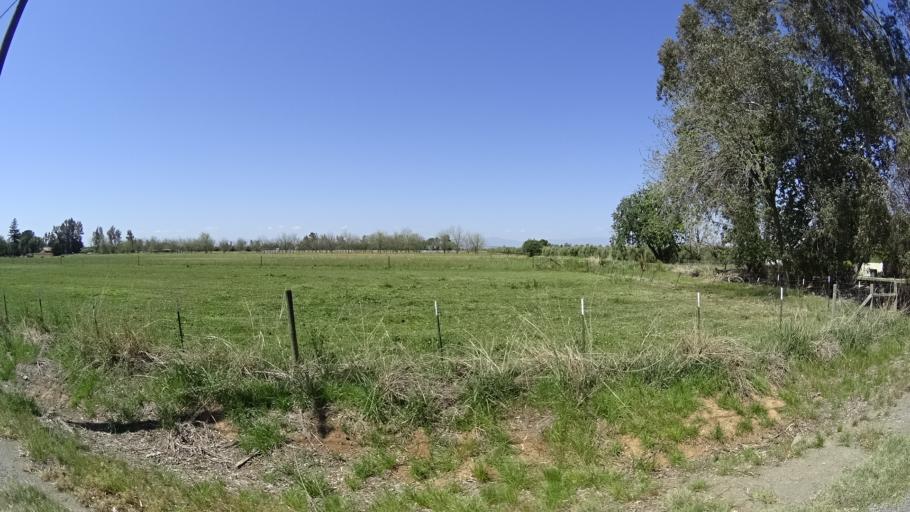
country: US
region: California
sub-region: Glenn County
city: Orland
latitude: 39.7725
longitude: -122.1783
